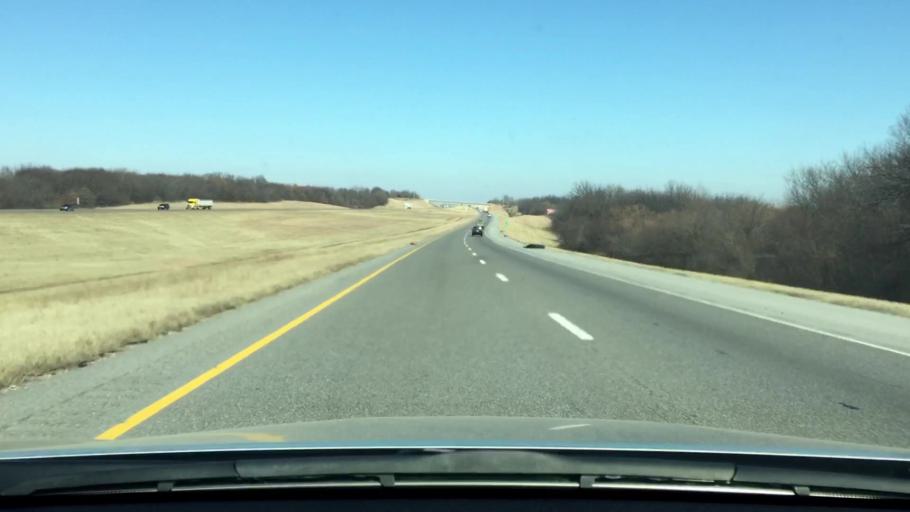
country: US
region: Oklahoma
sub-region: McClain County
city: Purcell
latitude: 34.9482
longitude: -97.3683
